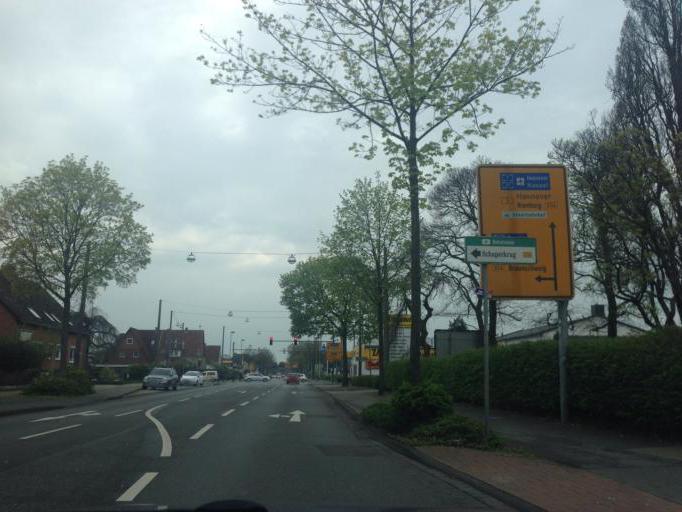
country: DE
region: Lower Saxony
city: Celle
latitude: 52.6104
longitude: 10.0770
